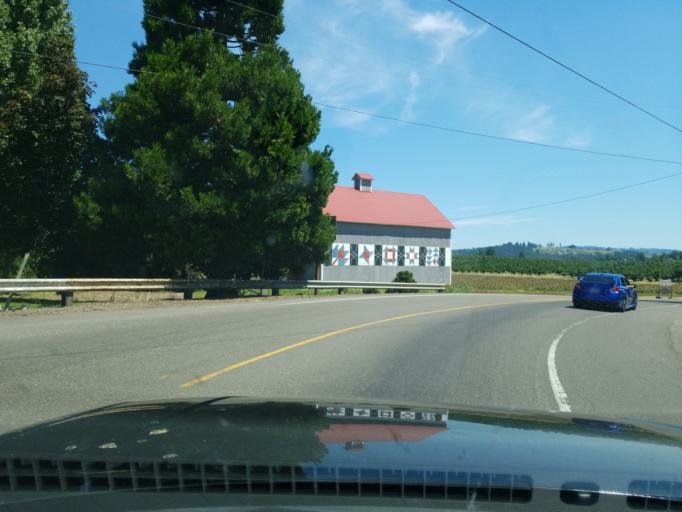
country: US
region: Oregon
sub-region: Yamhill County
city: Yamhill
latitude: 45.3457
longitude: -123.1876
